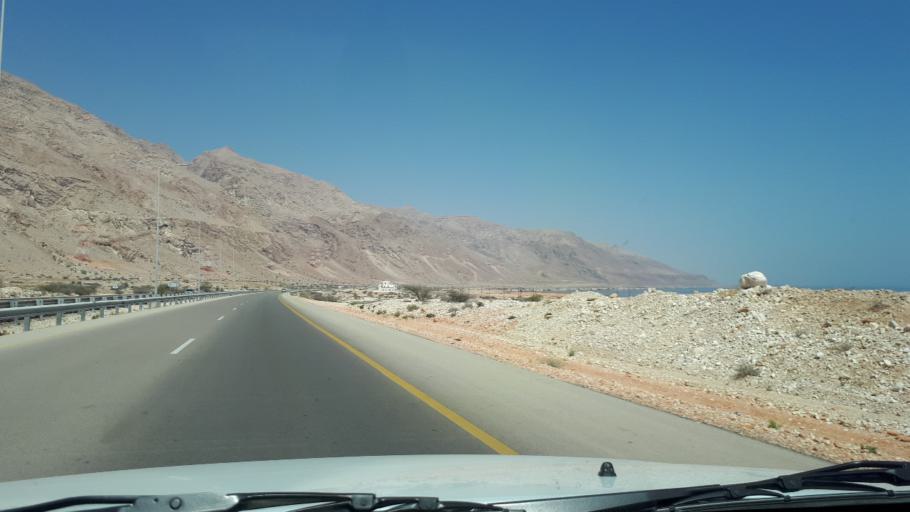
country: OM
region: Ash Sharqiyah
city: Sur
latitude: 22.7485
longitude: 59.3148
